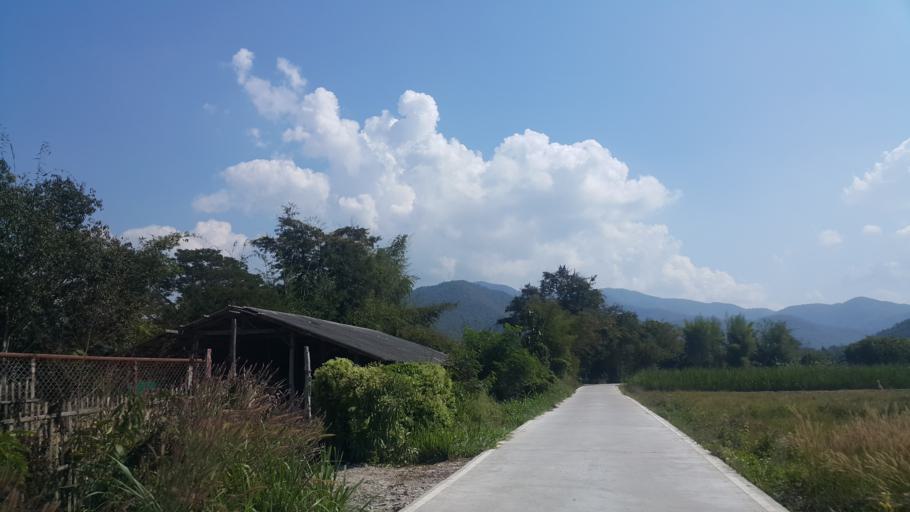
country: TH
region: Lamphun
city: Ban Thi
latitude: 18.6820
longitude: 99.1641
